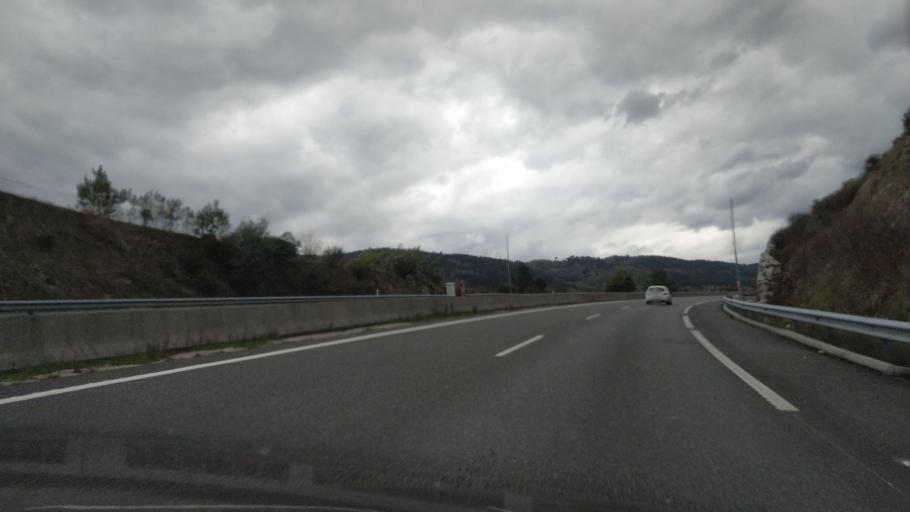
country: ES
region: Galicia
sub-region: Provincia de Ourense
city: Punxin
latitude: 42.3525
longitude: -7.9984
